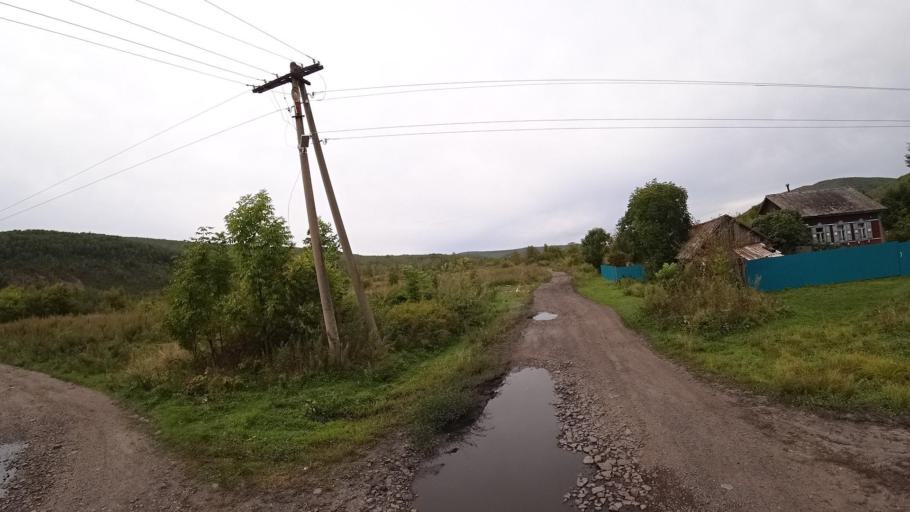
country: RU
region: Jewish Autonomous Oblast
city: Khingansk
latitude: 49.0408
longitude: 131.0498
